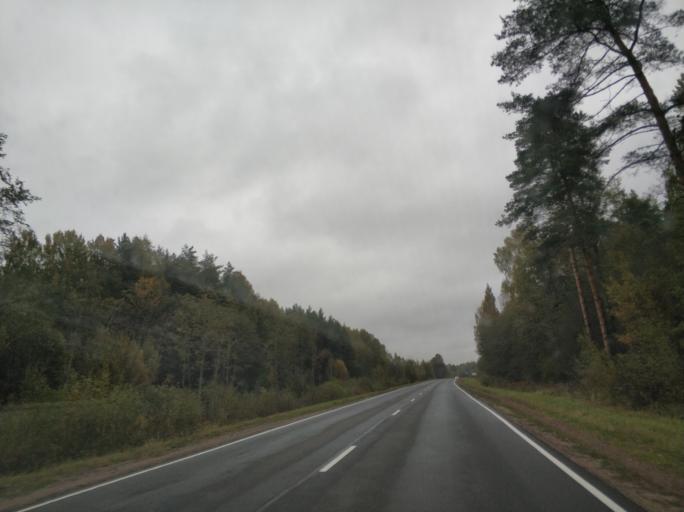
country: BY
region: Vitebsk
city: Rasony
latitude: 56.0948
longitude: 28.7219
